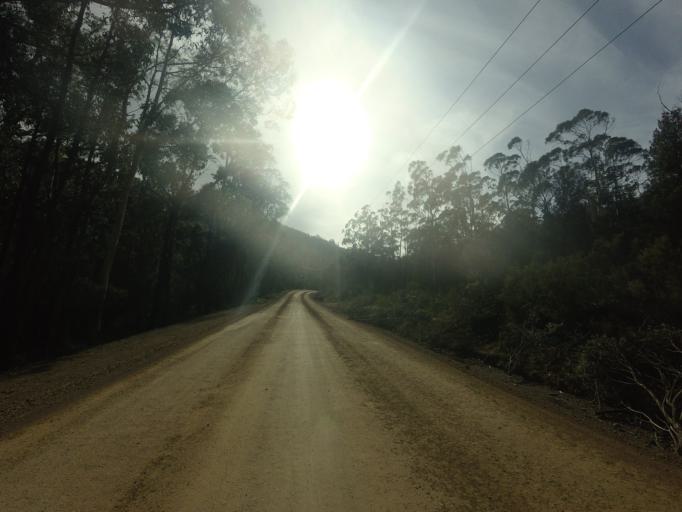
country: AU
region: Tasmania
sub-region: Huon Valley
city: Huonville
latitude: -43.0606
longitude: 147.0948
